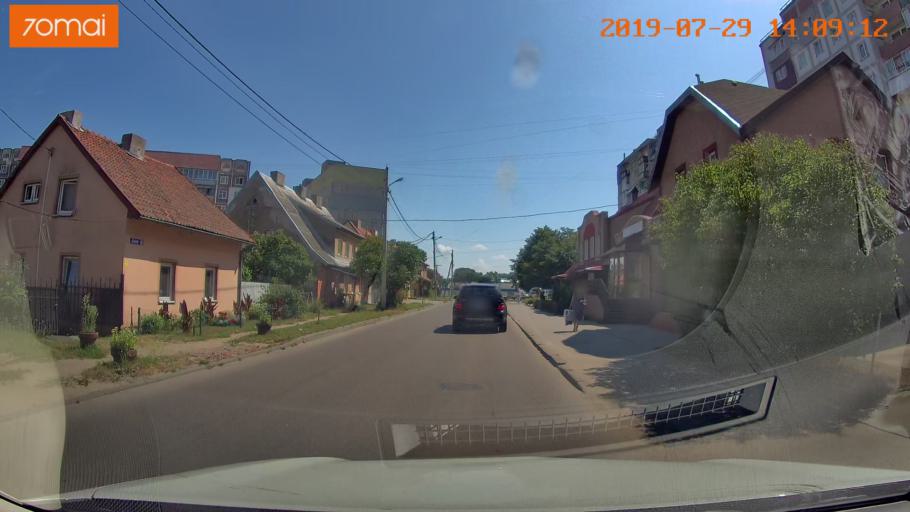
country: RU
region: Kaliningrad
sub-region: Gorod Kaliningrad
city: Baltiysk
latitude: 54.6560
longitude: 19.9088
